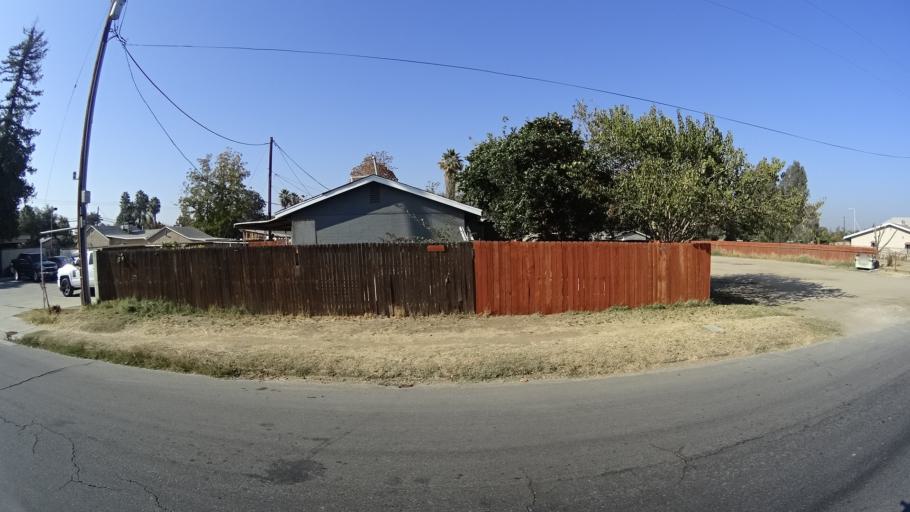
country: US
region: California
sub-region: Kern County
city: Bakersfield
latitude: 35.3511
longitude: -119.0214
